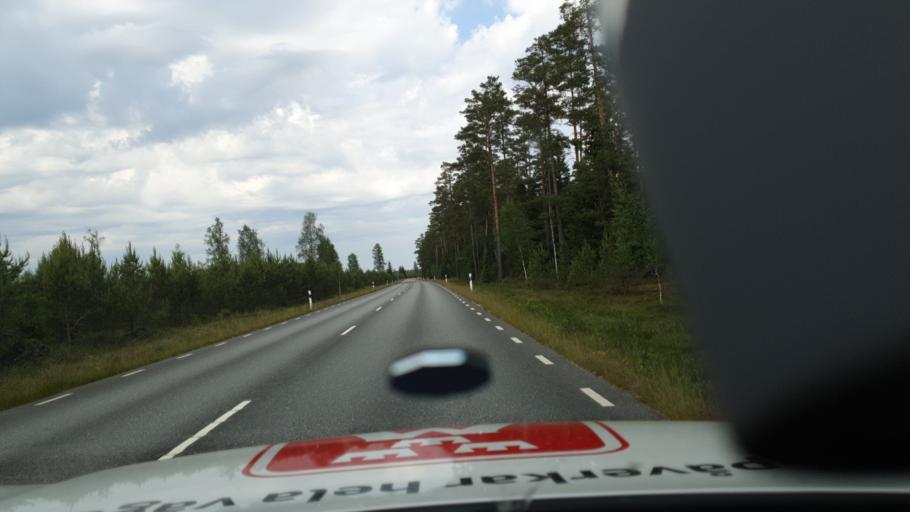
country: SE
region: Joenkoeping
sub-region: Varnamo Kommun
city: Varnamo
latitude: 57.3033
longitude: 14.0838
